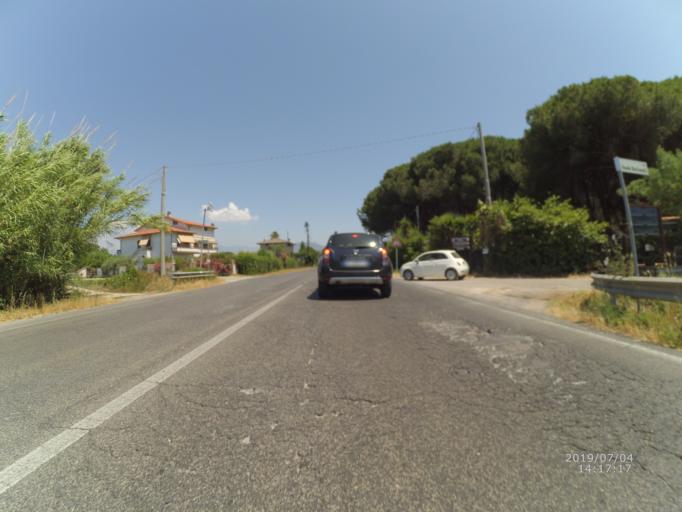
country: IT
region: Latium
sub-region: Provincia di Latina
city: Monte San Biagio
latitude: 41.2897
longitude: 13.3670
